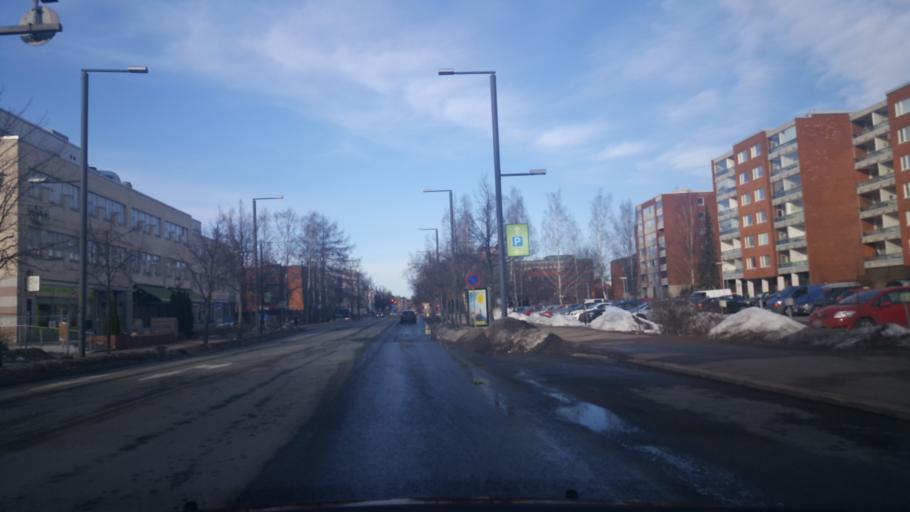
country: FI
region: Uusimaa
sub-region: Helsinki
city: Vantaa
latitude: 60.2909
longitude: 25.0364
